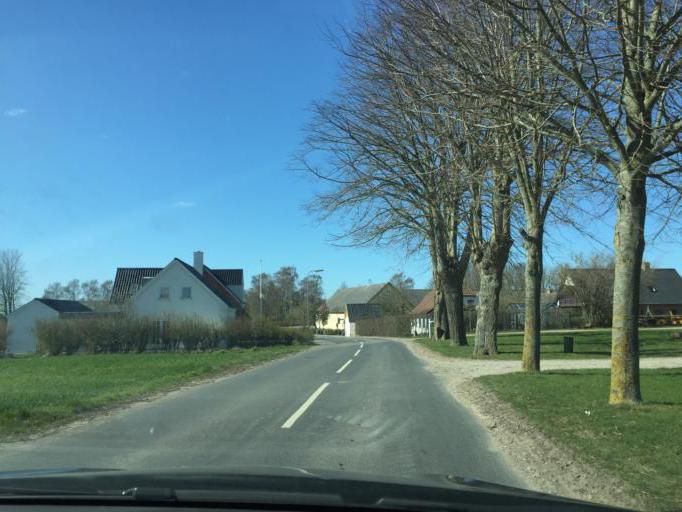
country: DK
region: South Denmark
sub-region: Faaborg-Midtfyn Kommune
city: Arslev
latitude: 55.3409
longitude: 10.4926
